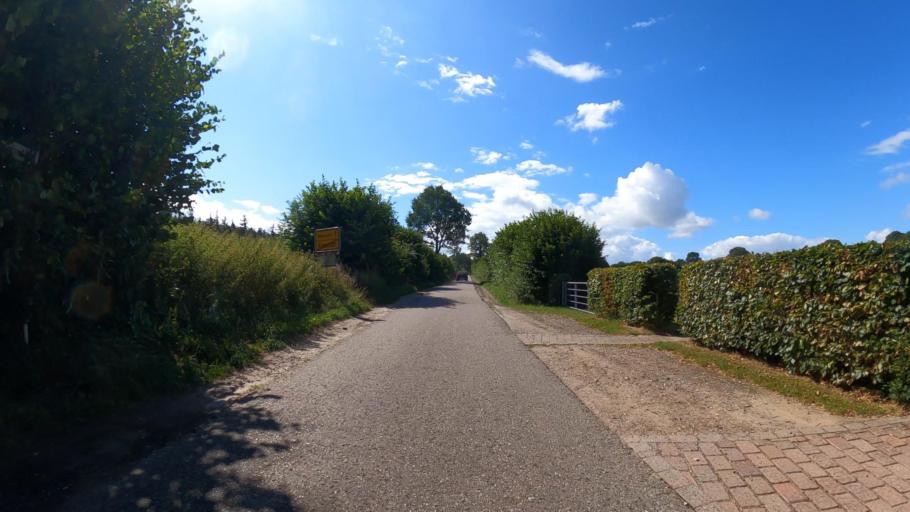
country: DE
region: Schleswig-Holstein
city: Armstedt
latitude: 53.9659
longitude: 9.8579
